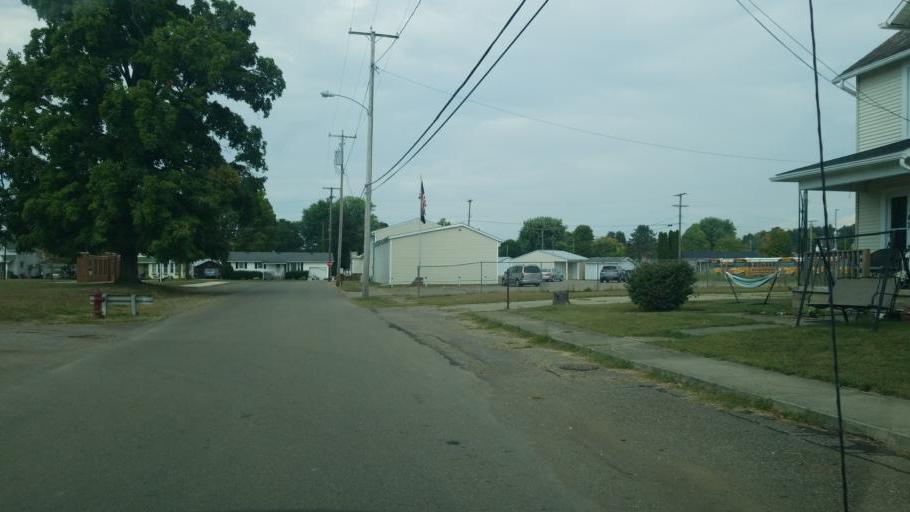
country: US
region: Ohio
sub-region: Licking County
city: Utica
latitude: 40.2332
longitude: -82.4492
